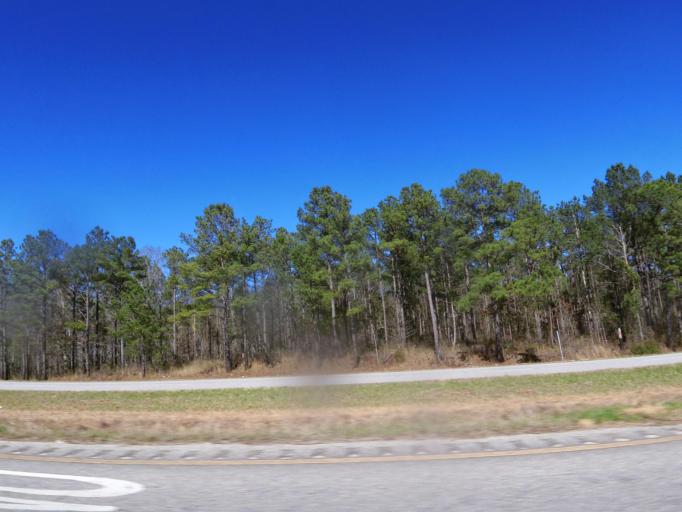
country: US
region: Alabama
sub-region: Bullock County
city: Union Springs
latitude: 32.1385
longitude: -85.6029
